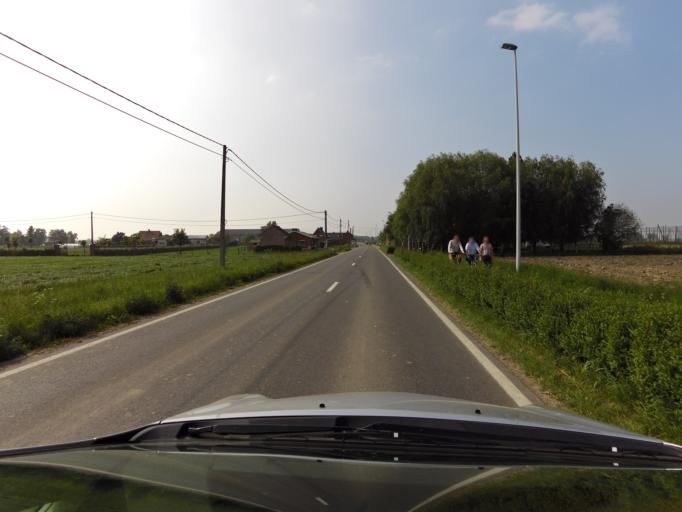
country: BE
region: Flanders
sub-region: Provincie West-Vlaanderen
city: Poperinge
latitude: 50.8701
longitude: 2.7119
